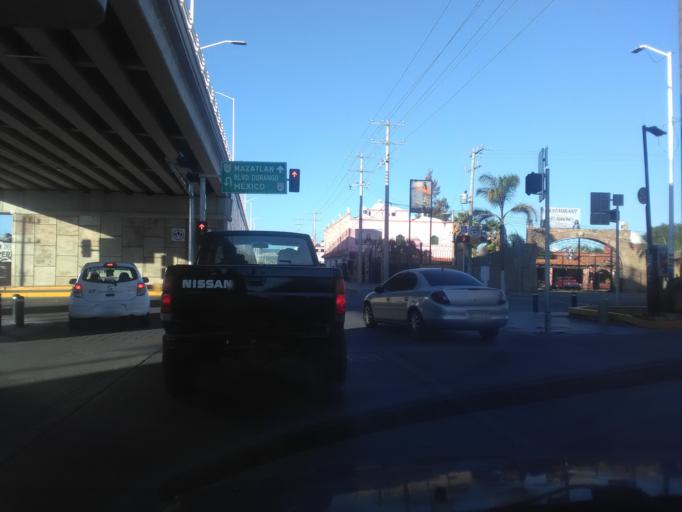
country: MX
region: Durango
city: Victoria de Durango
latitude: 24.0089
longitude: -104.6935
